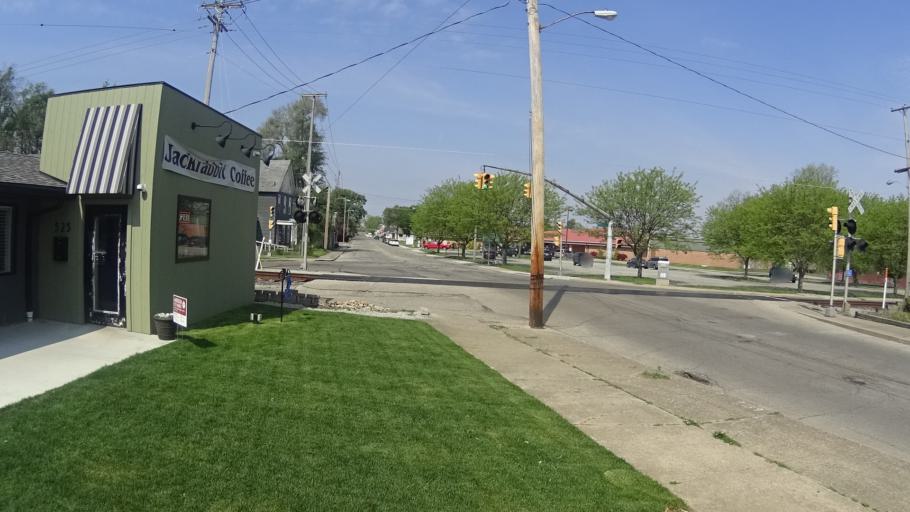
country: US
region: Indiana
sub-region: Madison County
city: Anderson
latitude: 40.1049
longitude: -85.6869
